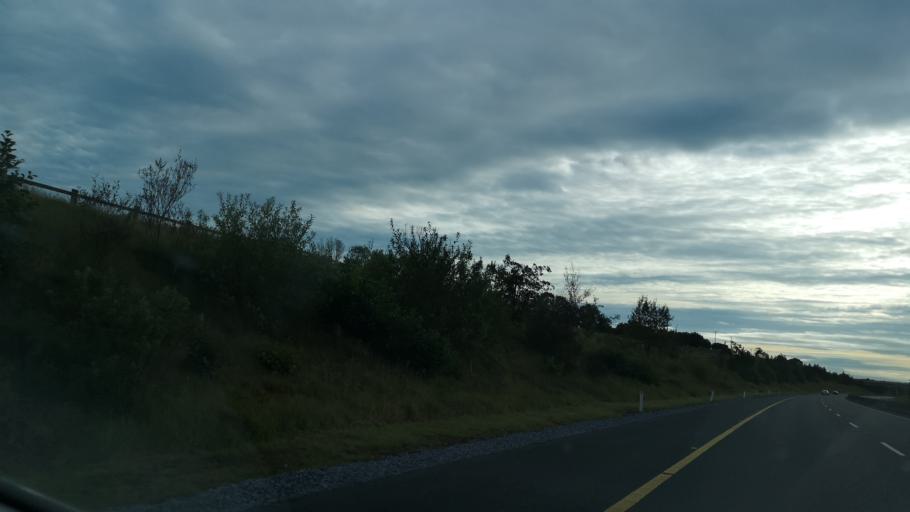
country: IE
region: Connaught
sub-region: County Galway
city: Loughrea
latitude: 53.2795
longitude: -8.5201
